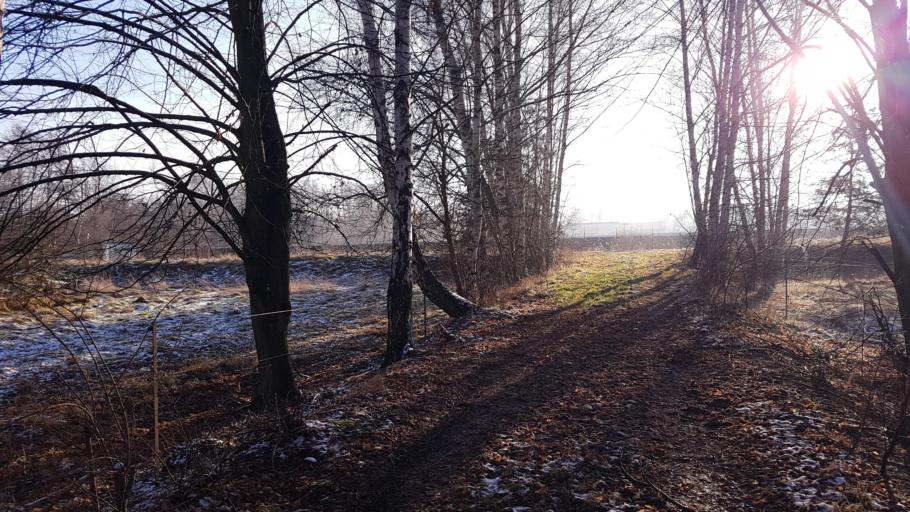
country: DE
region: Brandenburg
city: Doberlug-Kirchhain
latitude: 51.6311
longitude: 13.5822
